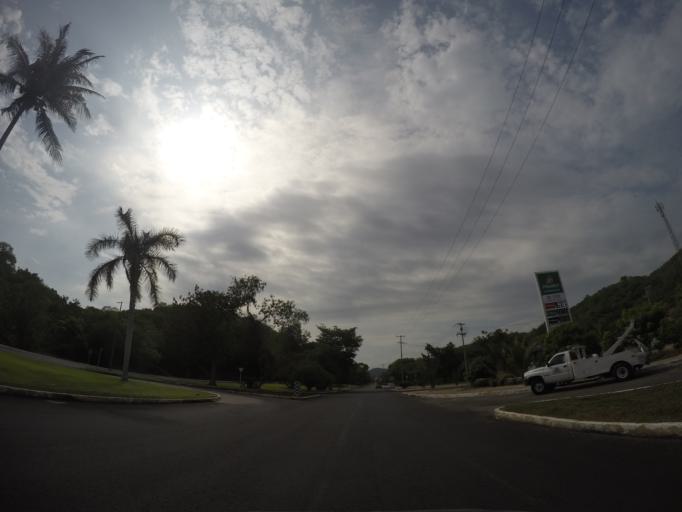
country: MX
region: Oaxaca
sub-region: Santa Maria Huatulco
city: Sector H Tres
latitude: 15.7726
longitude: -96.1457
